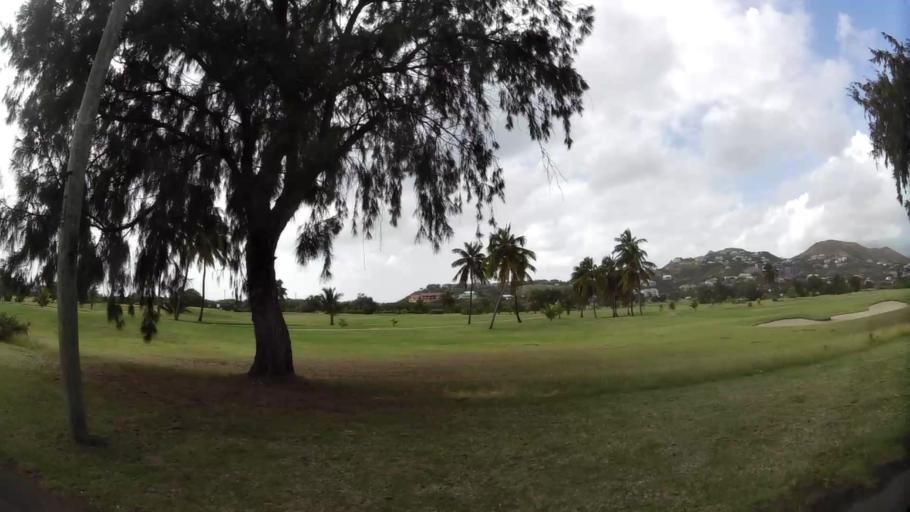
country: KN
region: Saint George Basseterre
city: Basseterre
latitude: 17.2853
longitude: -62.6853
